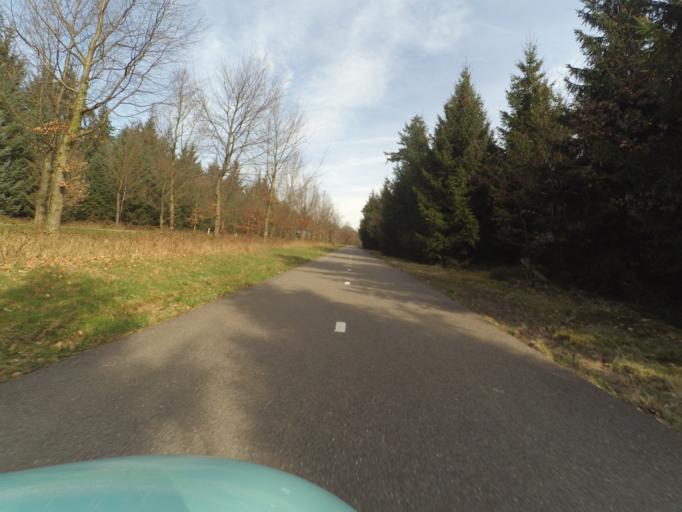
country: NL
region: Gelderland
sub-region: Gemeente Ede
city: Wekerom
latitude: 52.0831
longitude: 5.6953
